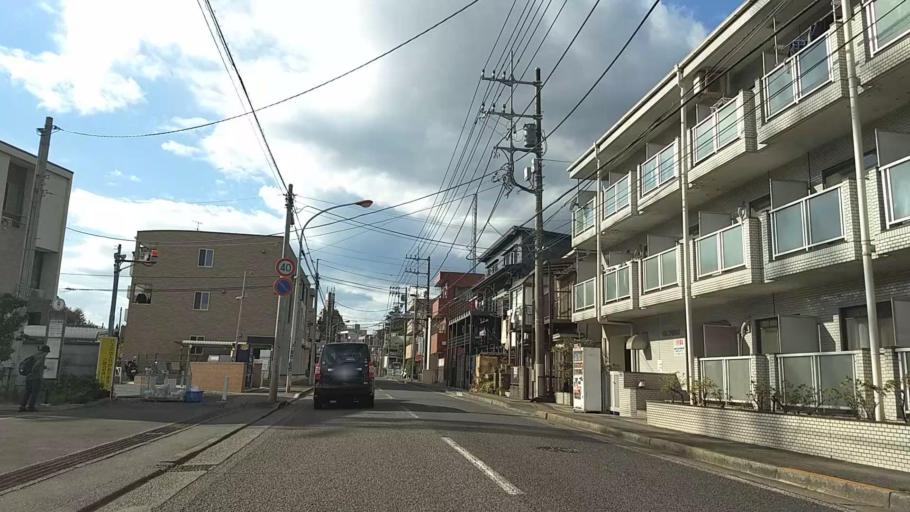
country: JP
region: Tokyo
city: Chofugaoka
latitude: 35.6150
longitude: 139.5343
